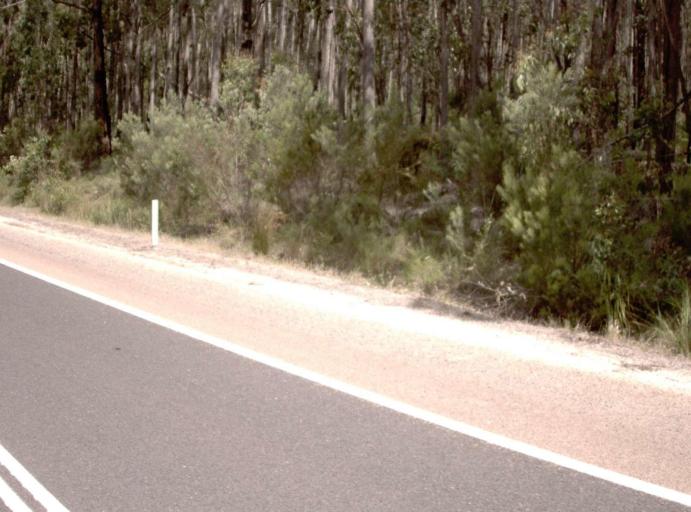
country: AU
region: New South Wales
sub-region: Bombala
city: Bombala
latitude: -37.5379
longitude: 149.4005
